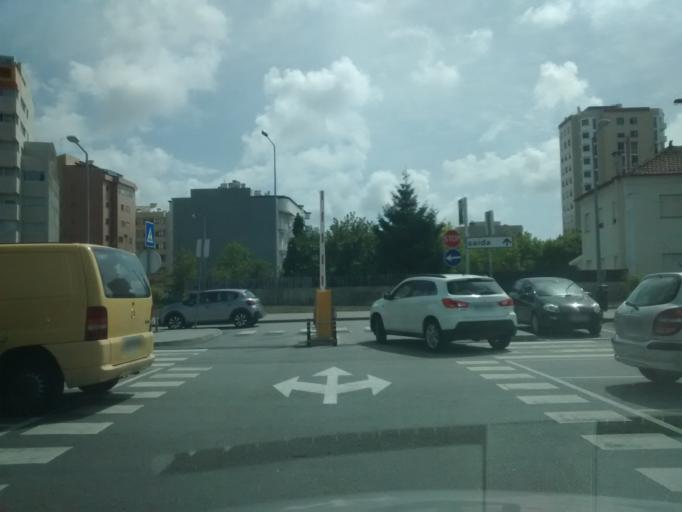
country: PT
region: Aveiro
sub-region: Aveiro
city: Aveiro
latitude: 40.6413
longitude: -8.6397
